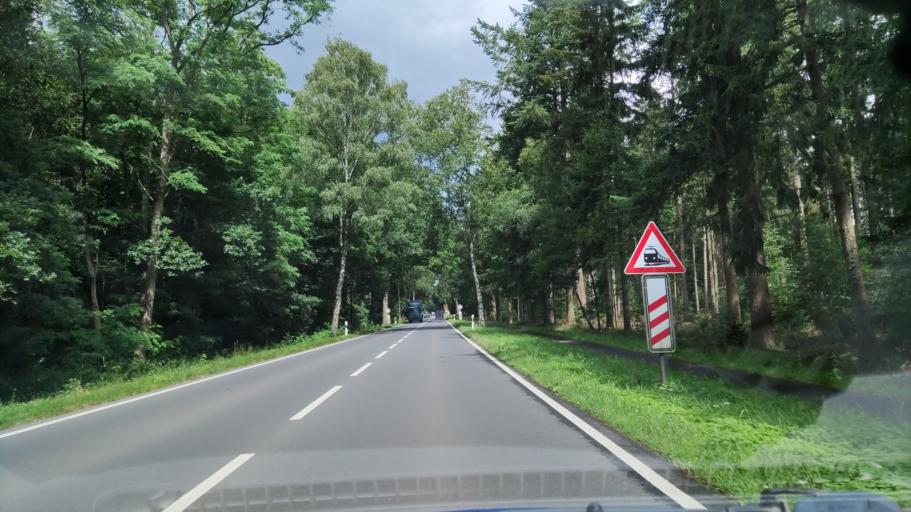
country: DE
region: Lower Saxony
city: Soltau
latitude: 52.9668
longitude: 9.8011
